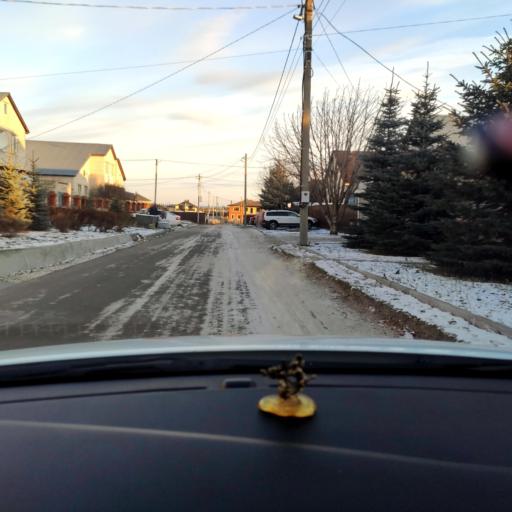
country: RU
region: Tatarstan
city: Stolbishchi
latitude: 55.6059
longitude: 49.1458
